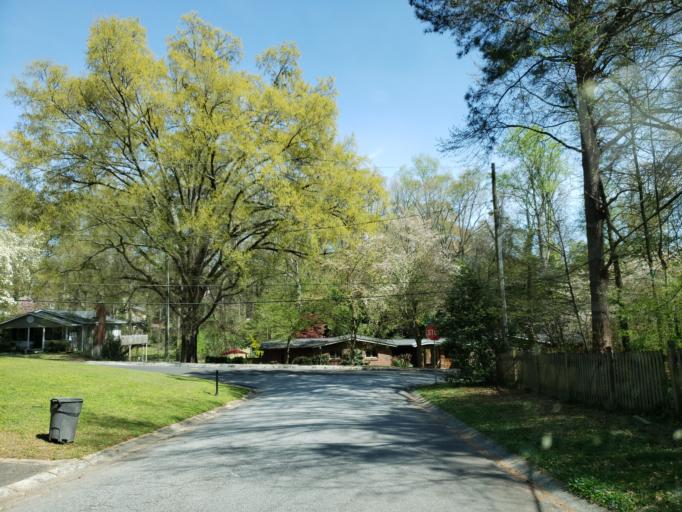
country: US
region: Georgia
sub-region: Cobb County
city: Marietta
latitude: 33.9583
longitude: -84.5603
